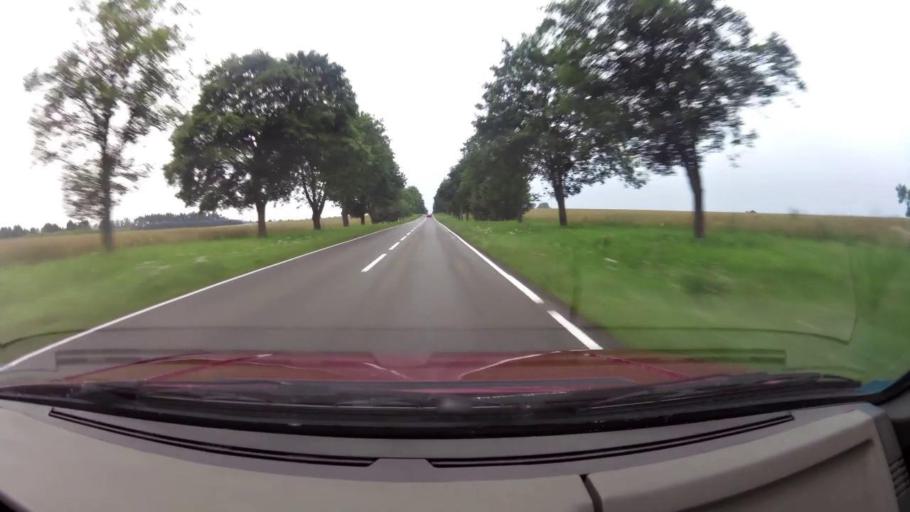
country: PL
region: West Pomeranian Voivodeship
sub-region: Powiat stargardzki
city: Stara Dabrowa
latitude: 53.3915
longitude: 15.1928
